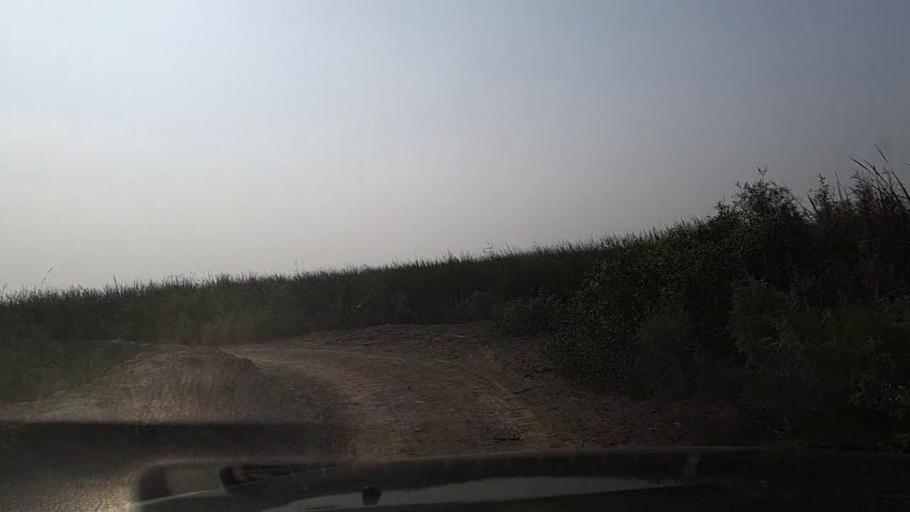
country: PK
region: Sindh
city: Mirpur Batoro
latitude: 24.6474
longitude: 68.2828
